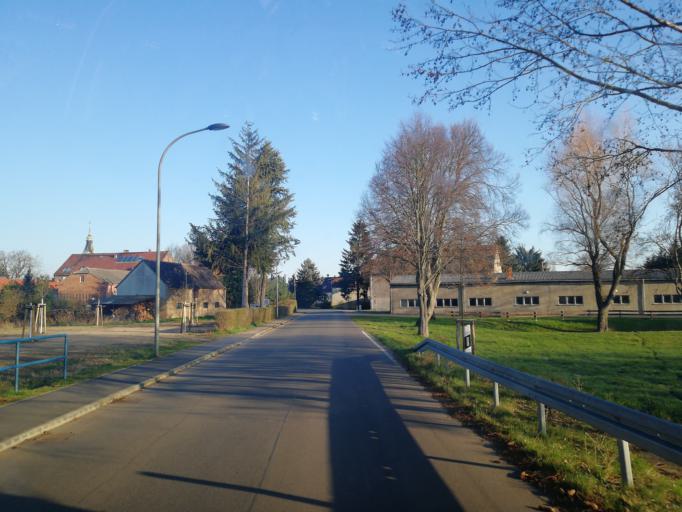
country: DE
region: Brandenburg
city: Drahnsdorf
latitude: 51.8726
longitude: 13.5916
